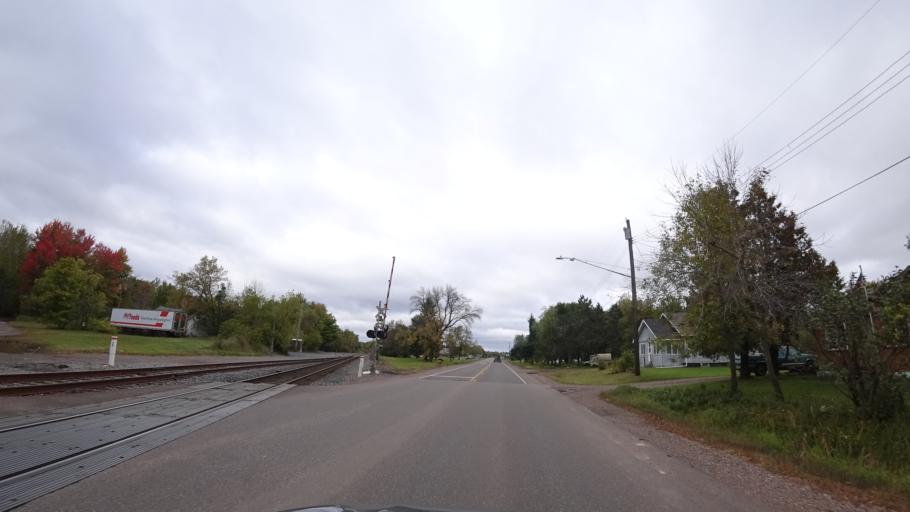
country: US
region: Wisconsin
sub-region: Rusk County
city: Ladysmith
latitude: 45.4736
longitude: -91.1108
